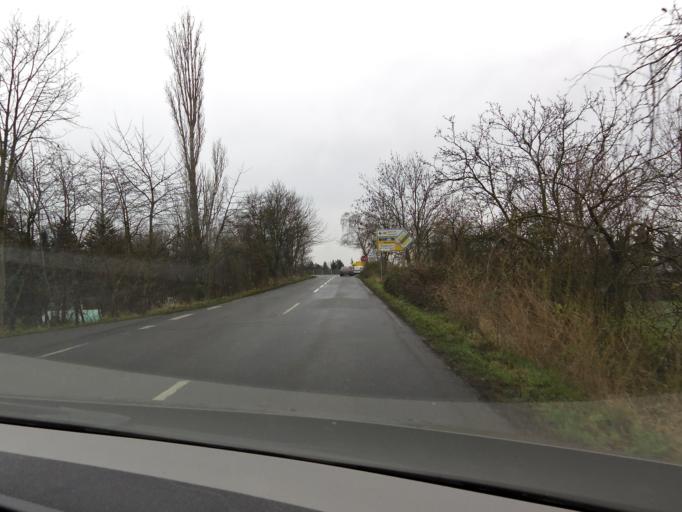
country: DE
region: Saxony
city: Markranstadt
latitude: 51.3452
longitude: 12.2838
